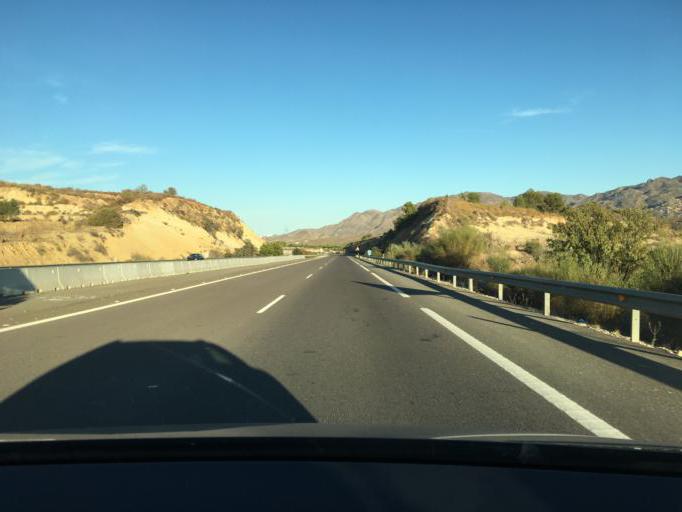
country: ES
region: Andalusia
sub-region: Provincia de Almeria
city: Bedar
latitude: 37.1458
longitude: -1.9699
